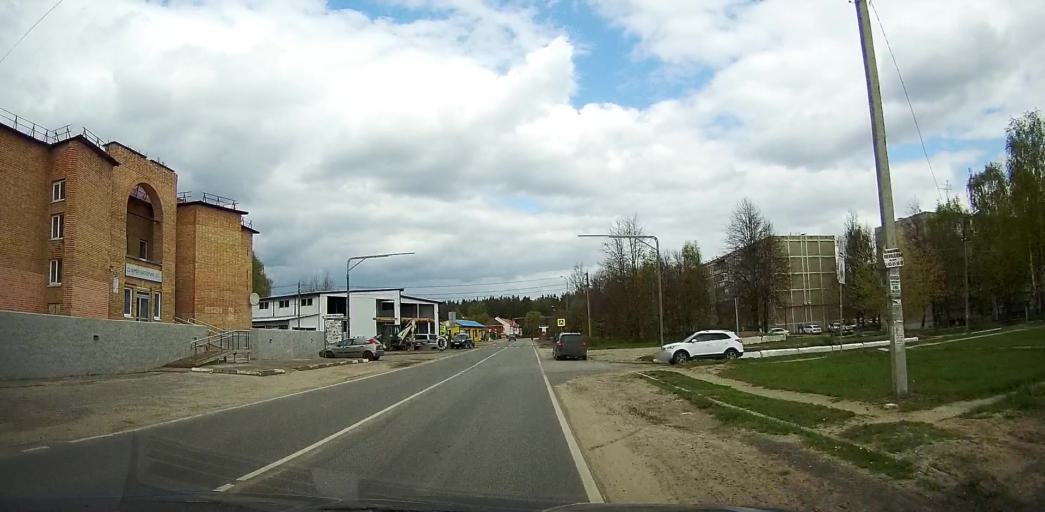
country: RU
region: Moskovskaya
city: Ashitkovo
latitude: 55.4364
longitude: 38.5792
